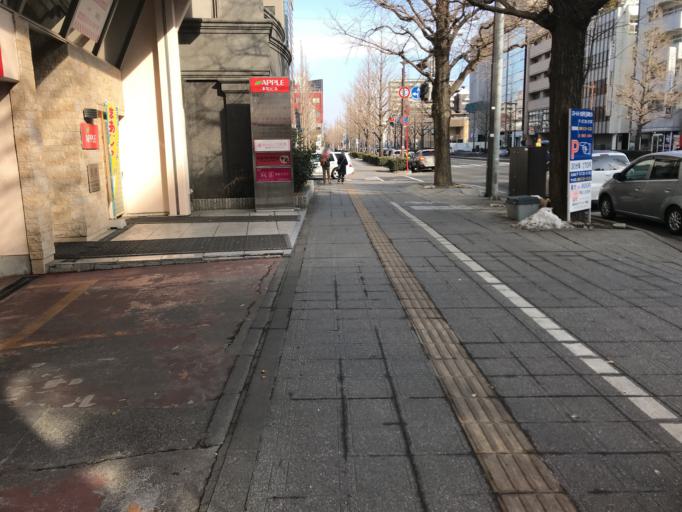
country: JP
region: Miyagi
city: Sendai-shi
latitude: 38.2694
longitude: 140.8746
